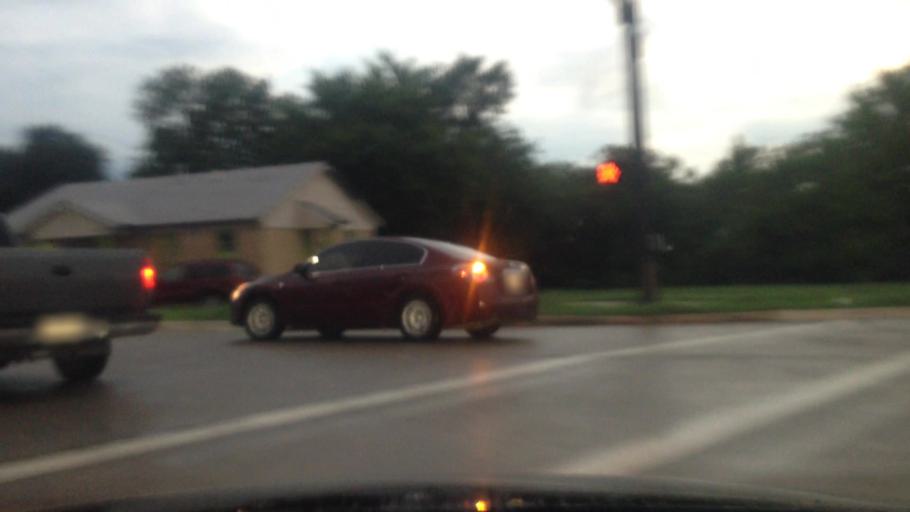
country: US
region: Texas
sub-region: Tarrant County
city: Arlington
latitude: 32.7355
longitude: -97.0840
